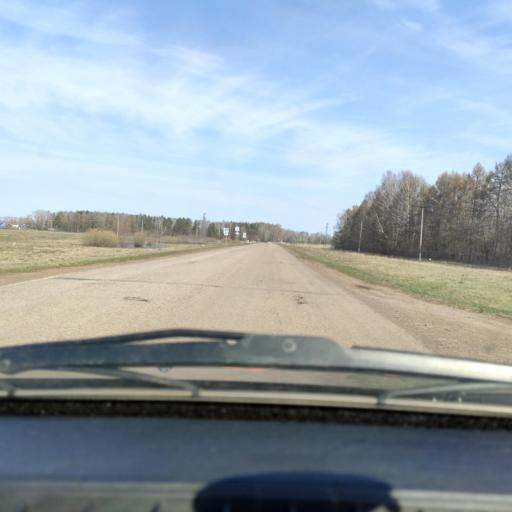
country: RU
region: Bashkortostan
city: Asanovo
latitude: 54.7677
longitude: 55.4871
